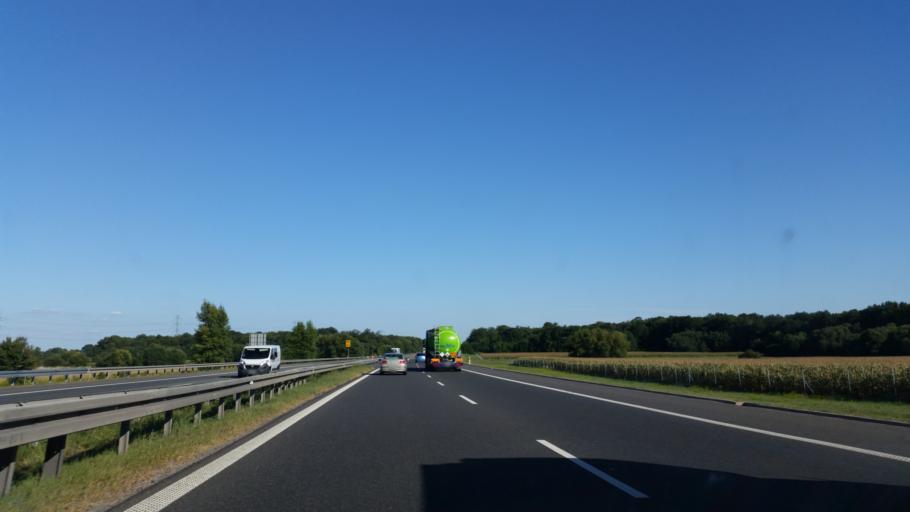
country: PL
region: Opole Voivodeship
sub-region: Powiat brzeski
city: Olszanka
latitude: 50.7332
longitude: 17.4997
